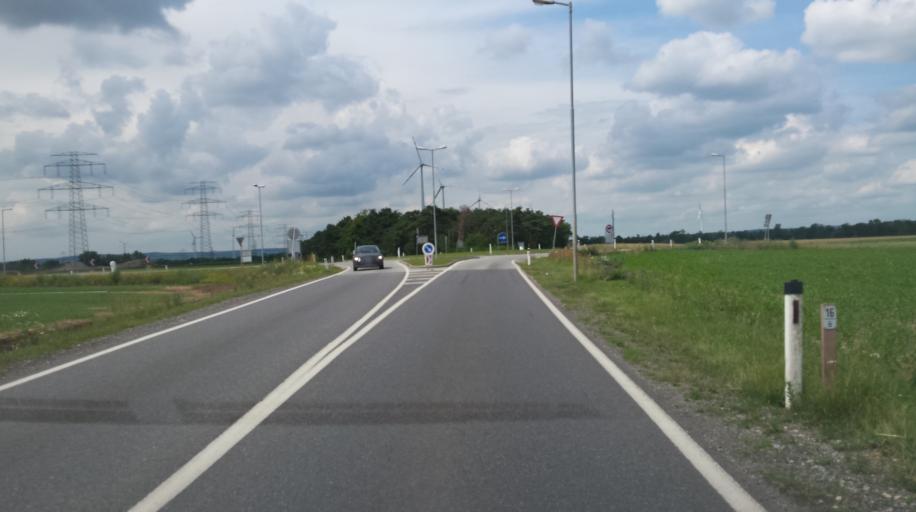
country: AT
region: Lower Austria
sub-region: Politischer Bezirk Mistelbach
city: Pillichsdorf
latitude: 48.3217
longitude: 16.5300
